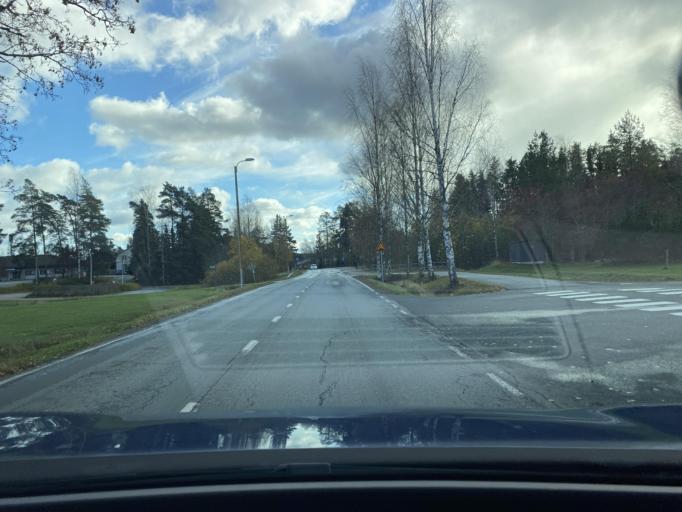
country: FI
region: Varsinais-Suomi
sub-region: Loimaa
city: Aura
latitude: 60.7214
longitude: 22.5999
